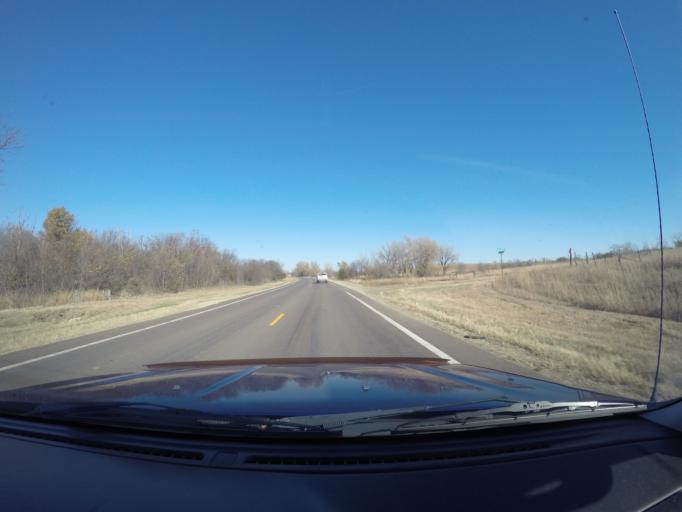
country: US
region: Kansas
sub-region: Marshall County
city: Blue Rapids
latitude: 39.5008
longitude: -96.7541
